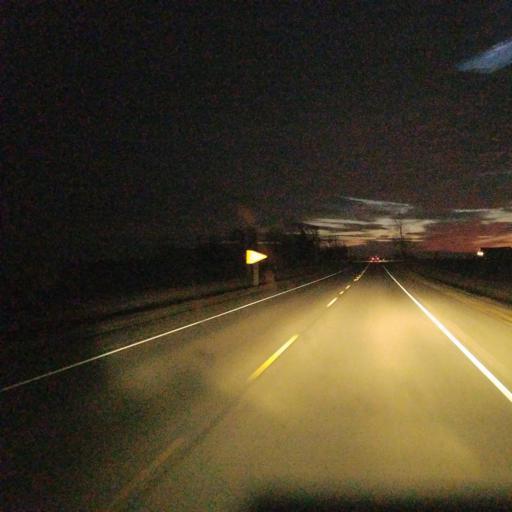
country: US
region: Illinois
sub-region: Fulton County
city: Farmington
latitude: 40.6982
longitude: -89.9370
